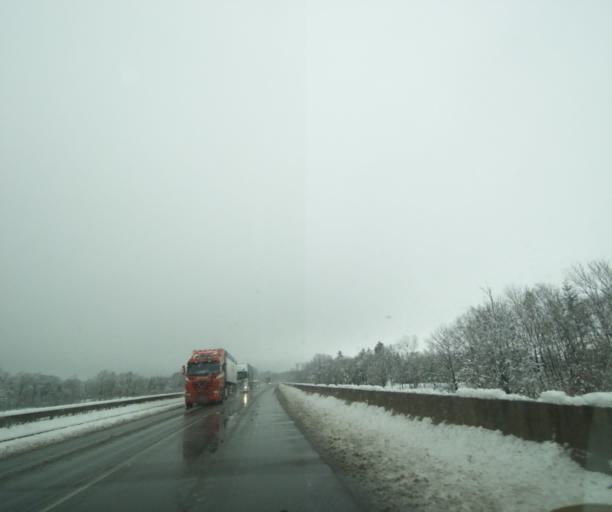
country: FR
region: Champagne-Ardenne
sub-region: Departement de la Haute-Marne
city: Villiers-en-Lieu
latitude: 48.5765
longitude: 4.8706
